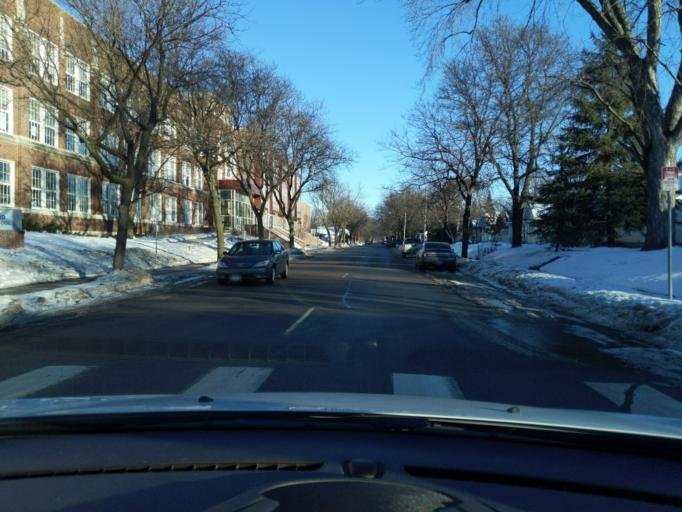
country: US
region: Minnesota
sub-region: Ramsey County
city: Lauderdale
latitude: 44.9379
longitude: -93.2128
